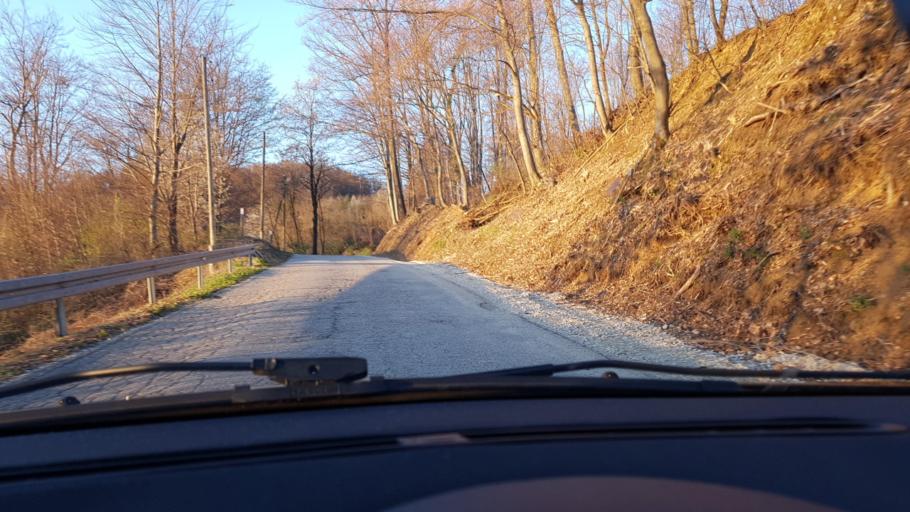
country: SI
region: Rogatec
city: Rogatec
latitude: 46.1772
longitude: 15.6822
